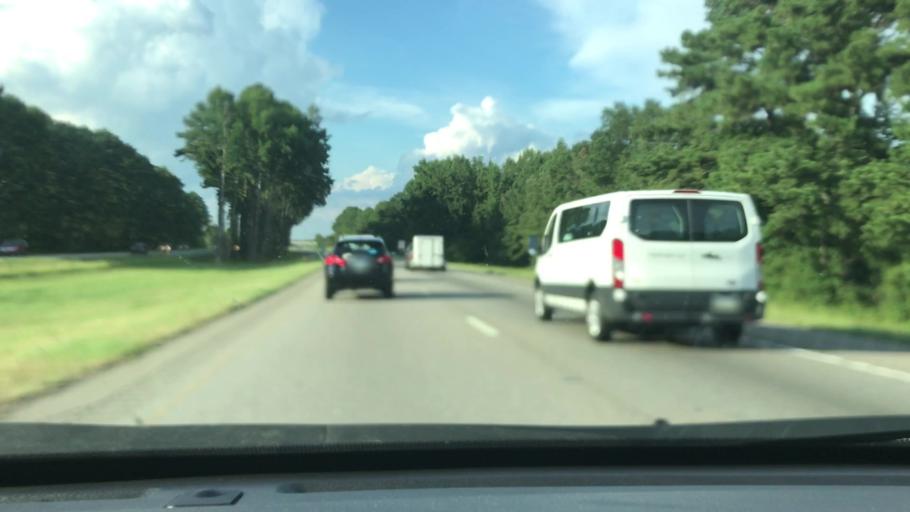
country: US
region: North Carolina
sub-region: Robeson County
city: Saint Pauls
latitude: 34.8399
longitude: -78.9735
